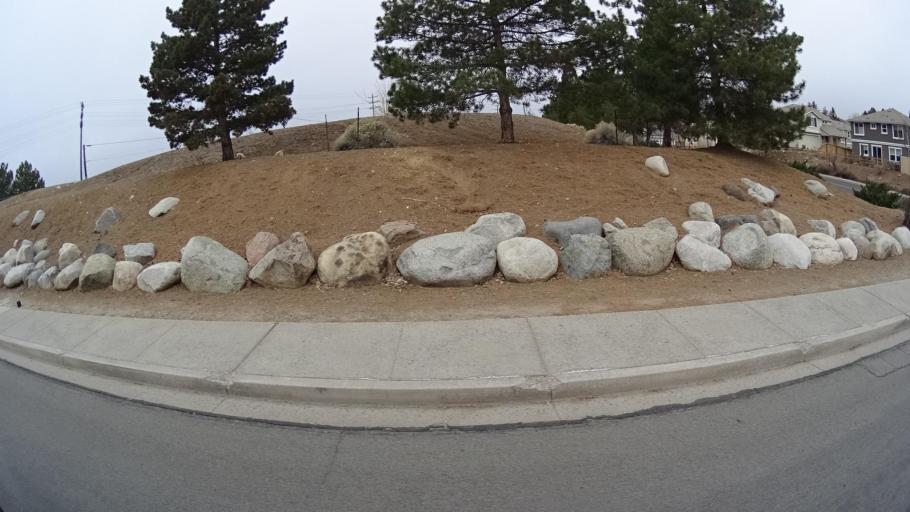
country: US
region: Nevada
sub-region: Washoe County
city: Reno
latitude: 39.5429
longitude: -119.8265
